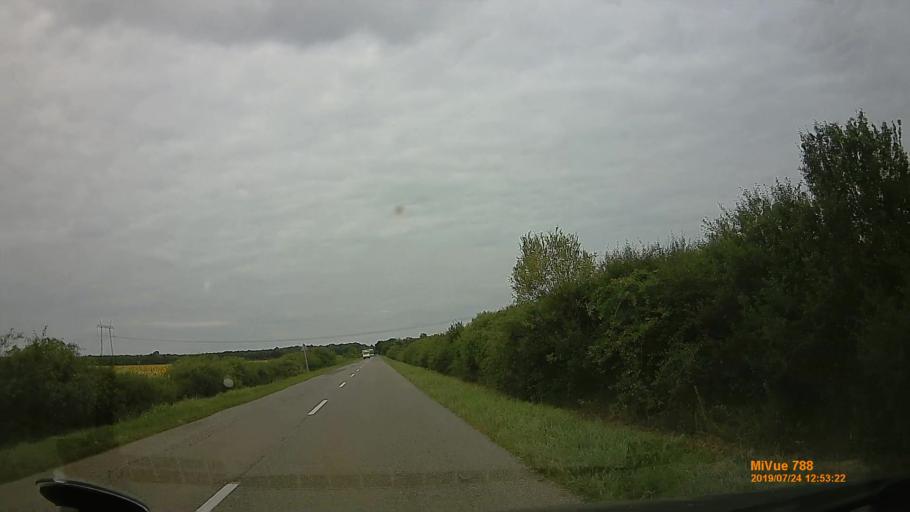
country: HU
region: Szabolcs-Szatmar-Bereg
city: Aranyosapati
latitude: 48.2043
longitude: 22.3071
